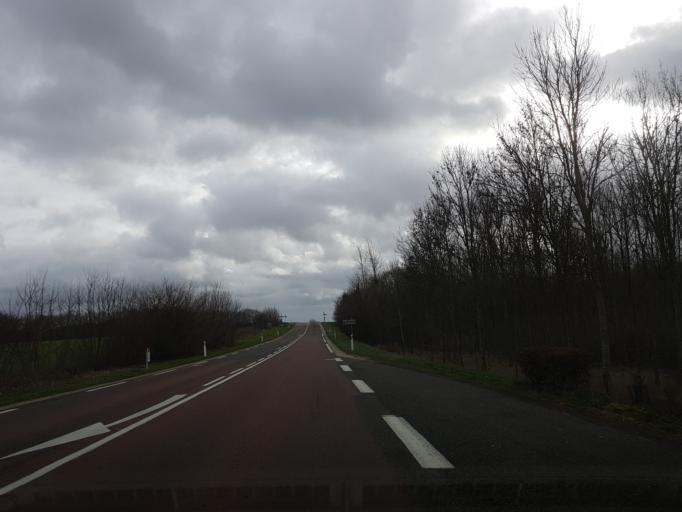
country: FR
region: Champagne-Ardenne
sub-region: Departement de la Haute-Marne
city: Chalindrey
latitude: 47.8384
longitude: 5.4679
